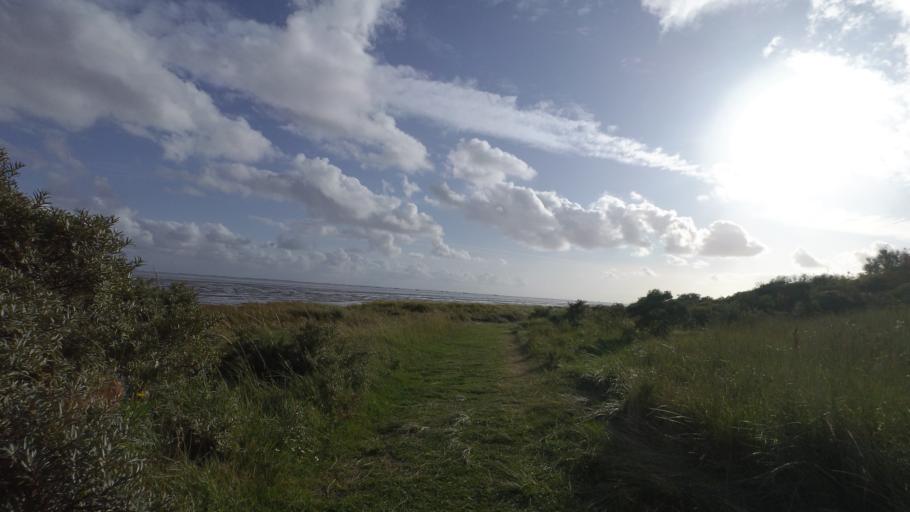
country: NL
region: Friesland
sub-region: Gemeente Dongeradeel
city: Holwerd
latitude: 53.4573
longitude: 5.9055
